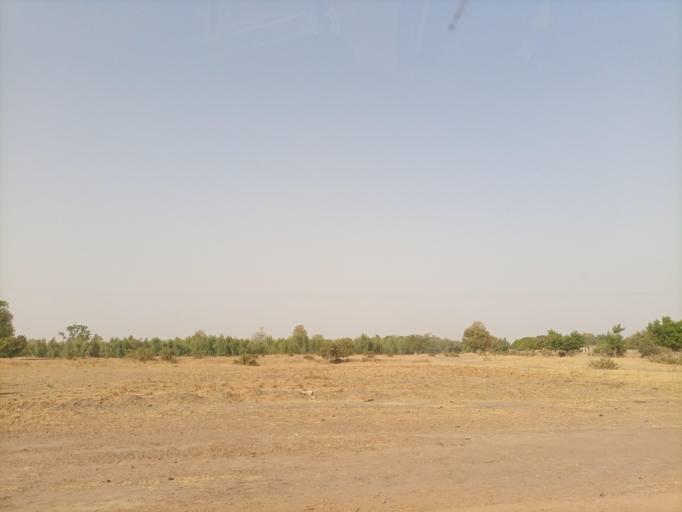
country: SN
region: Fatick
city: Passi
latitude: 14.0217
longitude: -16.2981
